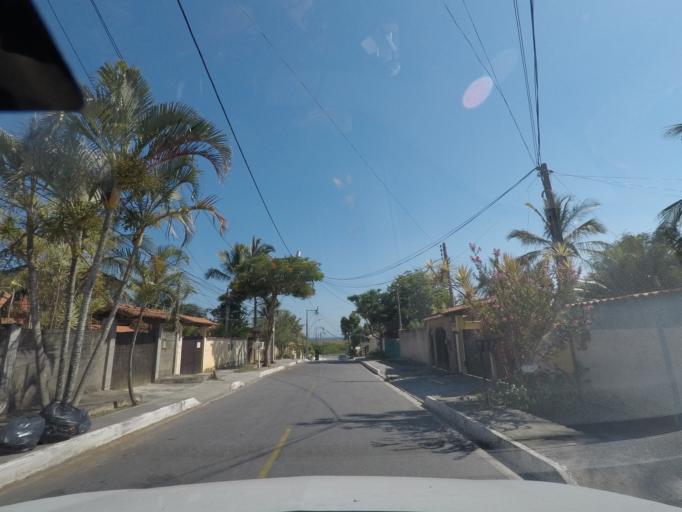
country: BR
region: Rio de Janeiro
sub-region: Niteroi
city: Niteroi
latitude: -22.9662
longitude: -42.9720
